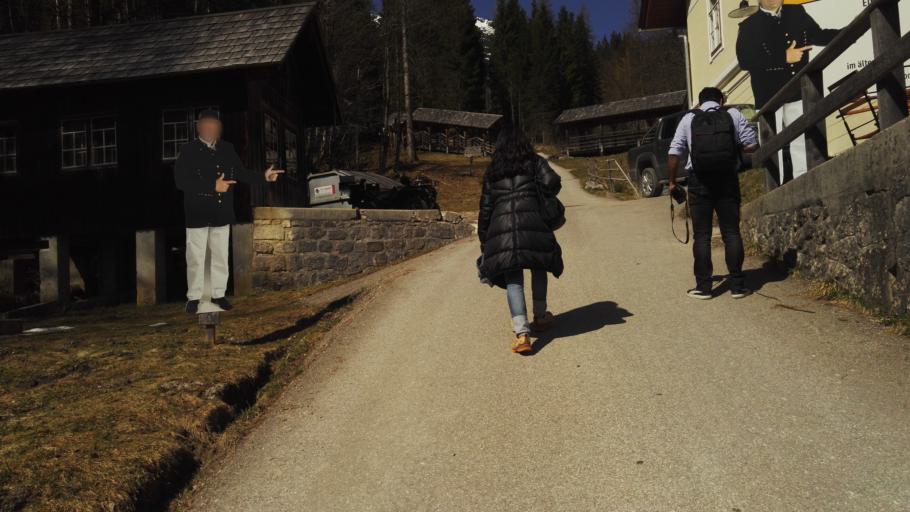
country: AT
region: Upper Austria
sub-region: Politischer Bezirk Gmunden
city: Bad Goisern
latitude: 47.5634
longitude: 13.6367
